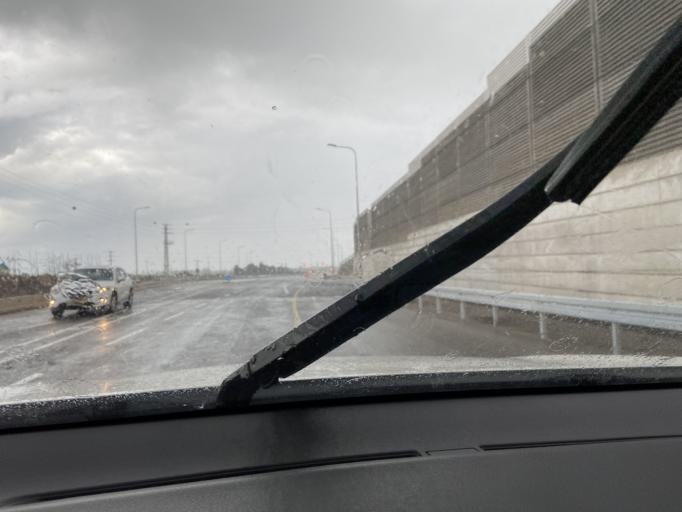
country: IL
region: Northern District
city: El Mazra`a
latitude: 32.9806
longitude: 35.0972
